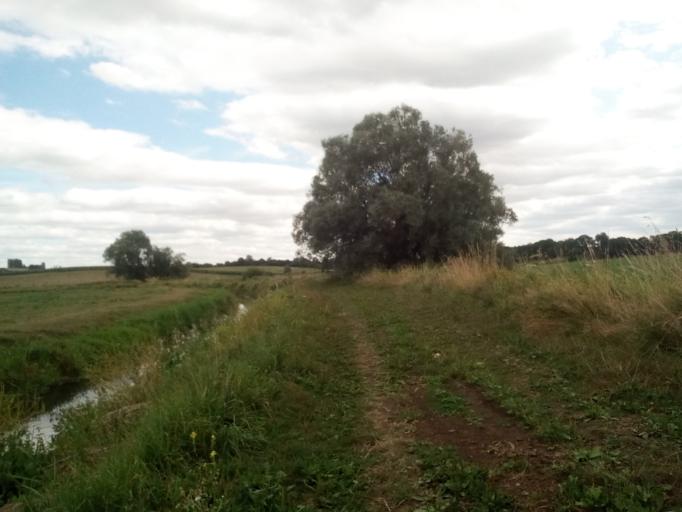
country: FR
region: Lower Normandy
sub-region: Departement du Calvados
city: Troarn
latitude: 49.1723
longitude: -0.1523
